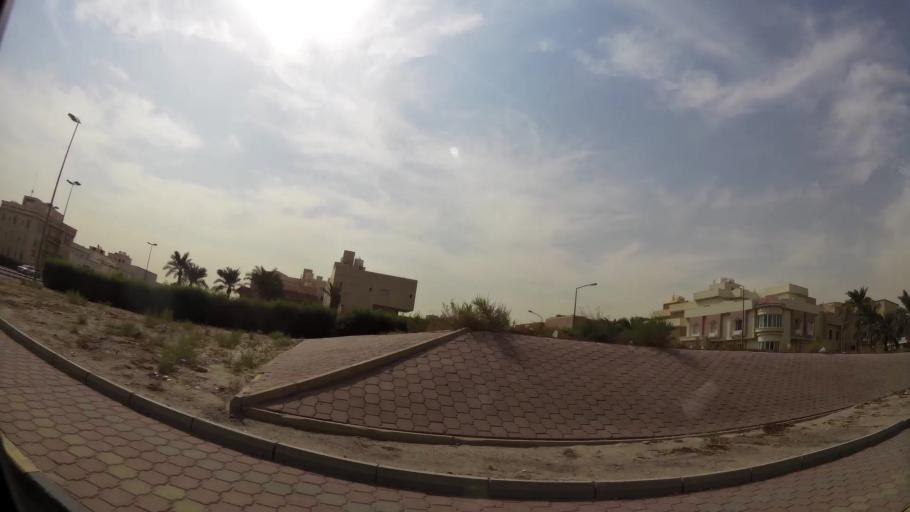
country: KW
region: Al Farwaniyah
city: Janub as Surrah
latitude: 29.2851
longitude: 47.9934
